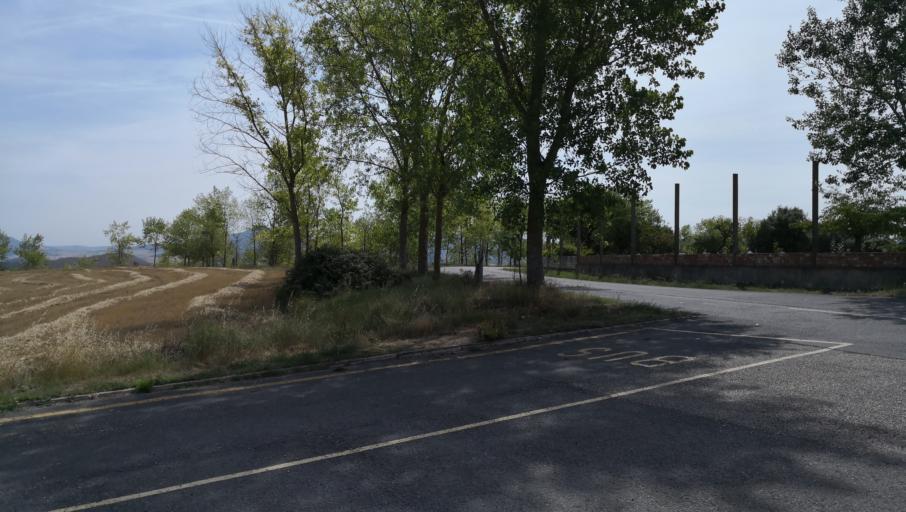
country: ES
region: Castille and Leon
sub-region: Provincia de Burgos
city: Miranda de Ebro
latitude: 42.6696
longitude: -2.9433
